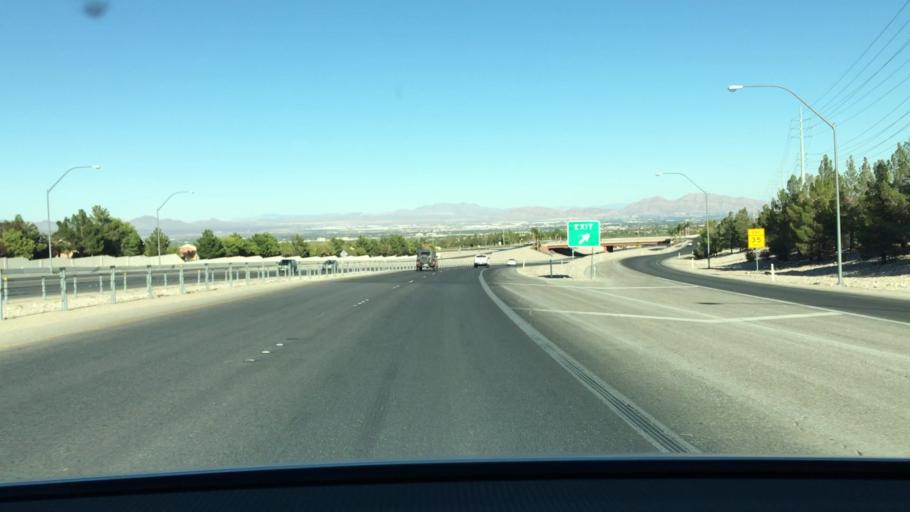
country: US
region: Nevada
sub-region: Clark County
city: Summerlin South
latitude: 36.1935
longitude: -115.3292
